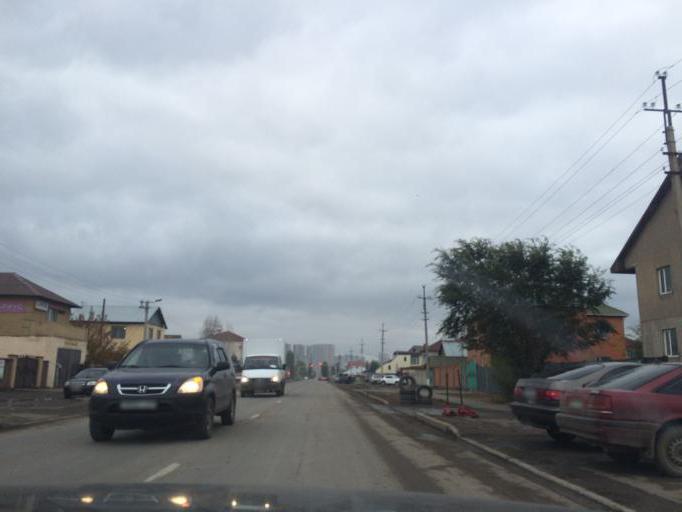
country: KZ
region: Astana Qalasy
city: Astana
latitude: 51.1350
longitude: 71.4973
